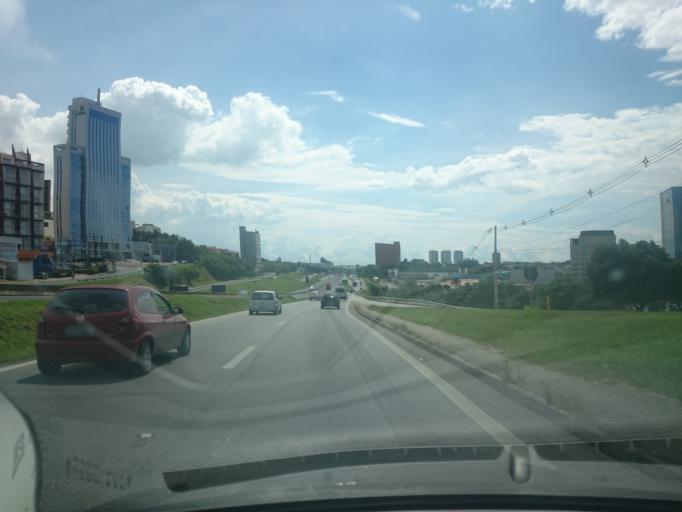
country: BR
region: Sao Paulo
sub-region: Sorocaba
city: Sorocaba
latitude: -23.5298
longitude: -47.4666
